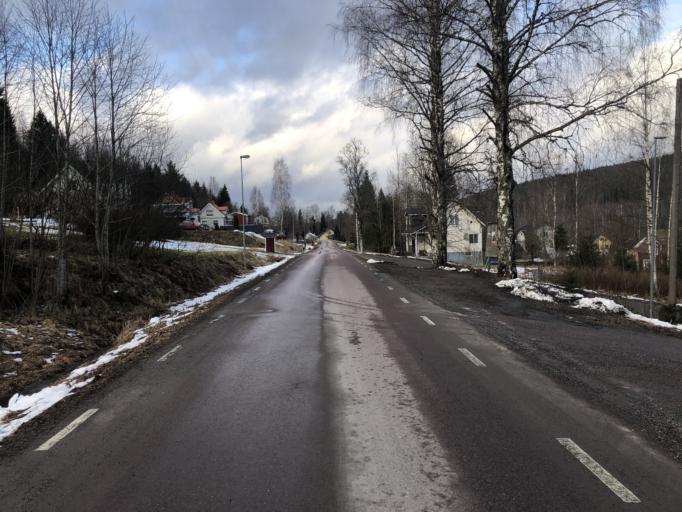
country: SE
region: Vaermland
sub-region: Filipstads Kommun
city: Lesjofors
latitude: 59.9695
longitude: 14.1869
